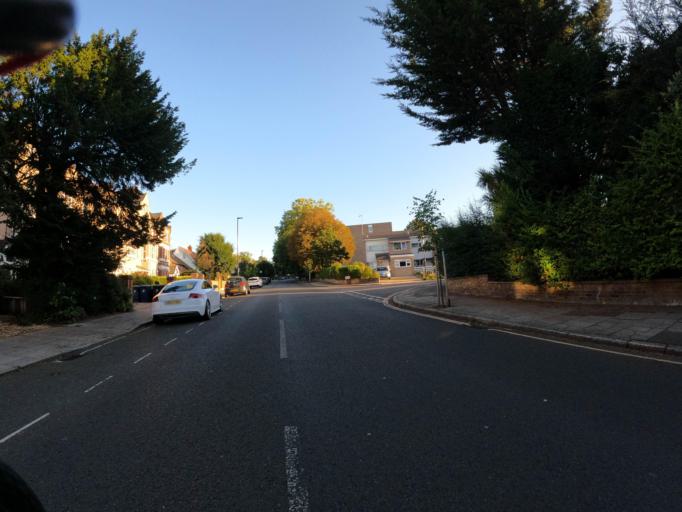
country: GB
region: England
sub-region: Greater London
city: Ealing Broadway
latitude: 51.5243
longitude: -0.3179
